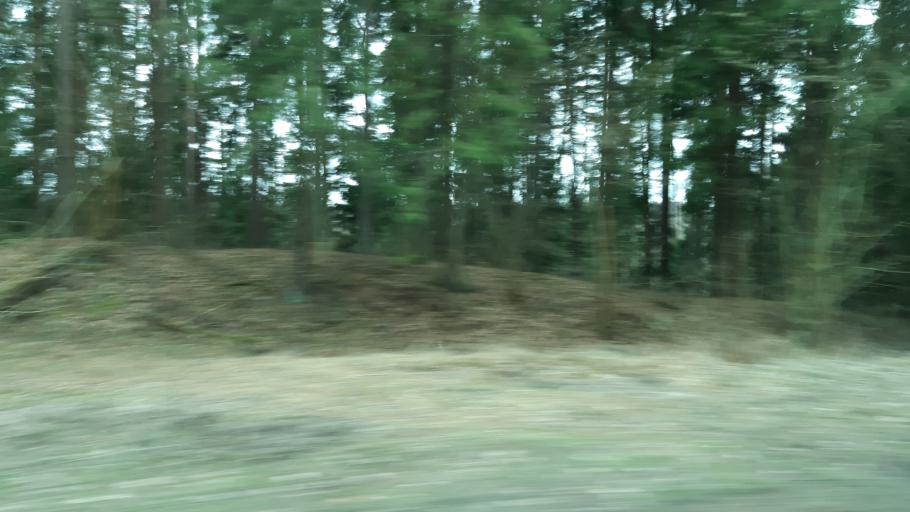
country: PL
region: Podlasie
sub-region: Suwalki
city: Suwalki
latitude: 54.3076
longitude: 22.9580
